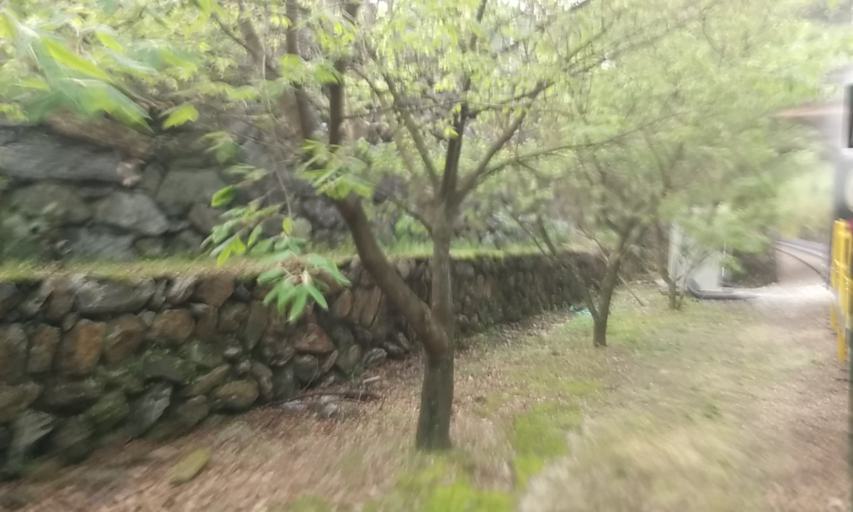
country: JP
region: Ehime
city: Niihama
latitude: 33.9011
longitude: 133.3089
